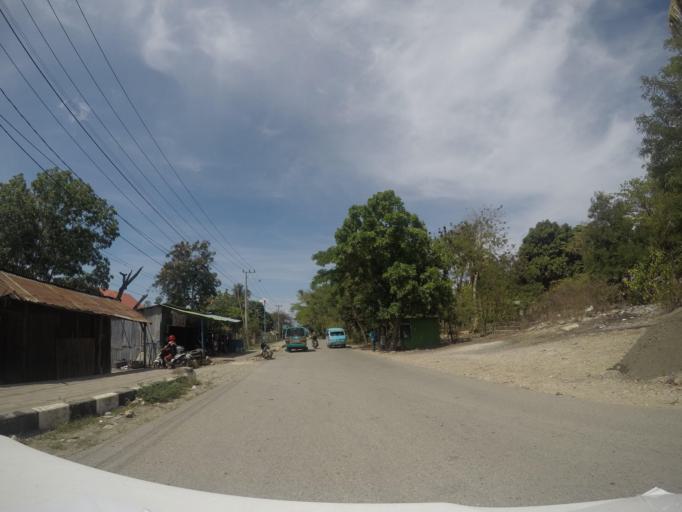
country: TL
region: Baucau
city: Baucau
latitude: -8.4700
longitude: 126.4590
